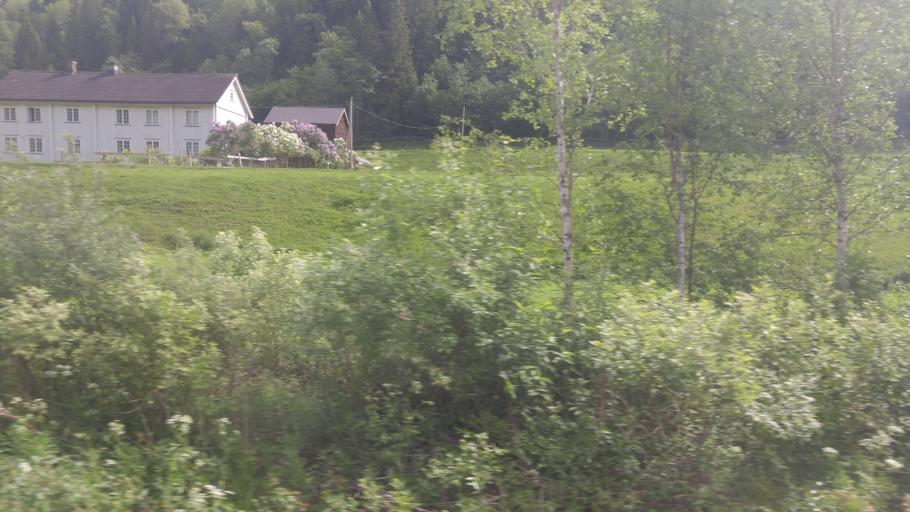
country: NO
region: Sor-Trondelag
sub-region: Midtre Gauldal
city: Storen
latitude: 63.0066
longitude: 10.4571
